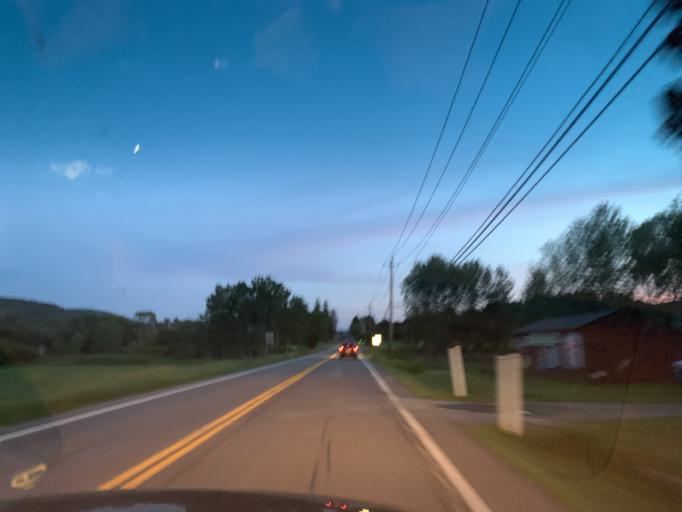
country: US
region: New York
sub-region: Chenango County
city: New Berlin
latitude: 42.5275
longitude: -75.3864
